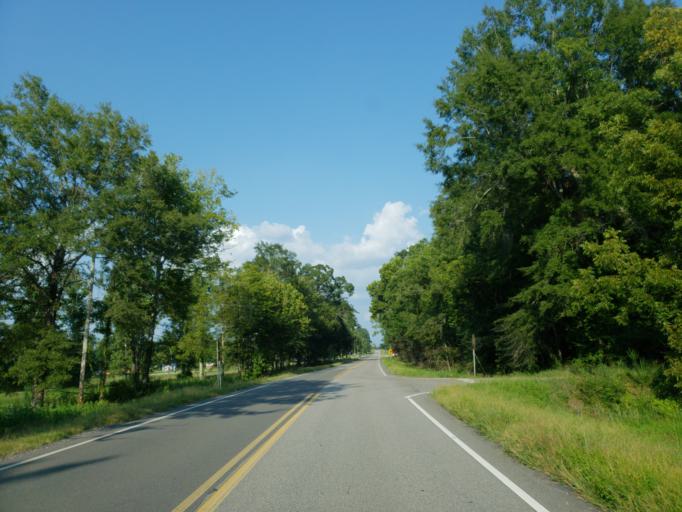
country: US
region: Alabama
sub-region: Greene County
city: Eutaw
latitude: 32.7545
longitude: -88.0314
